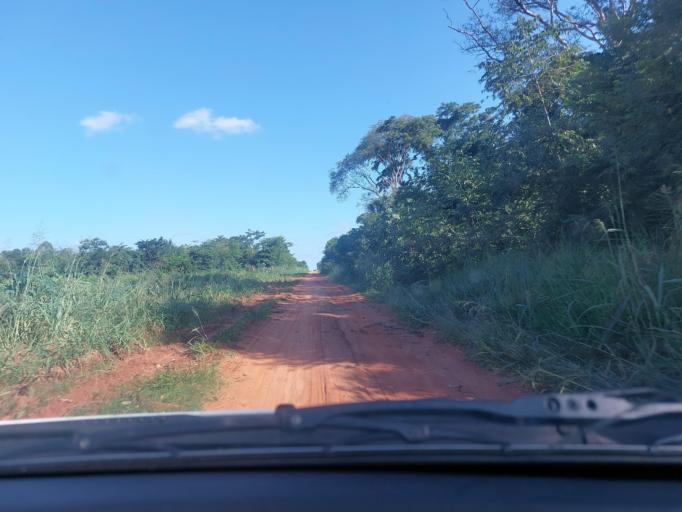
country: PY
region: San Pedro
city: Guayaybi
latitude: -24.5087
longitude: -56.5461
